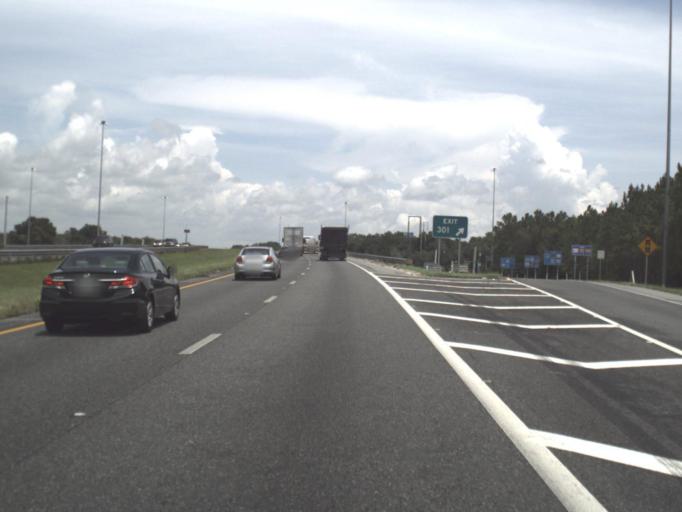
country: US
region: Florida
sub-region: Hernando County
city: Hill 'n Dale
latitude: 28.5199
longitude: -82.2371
